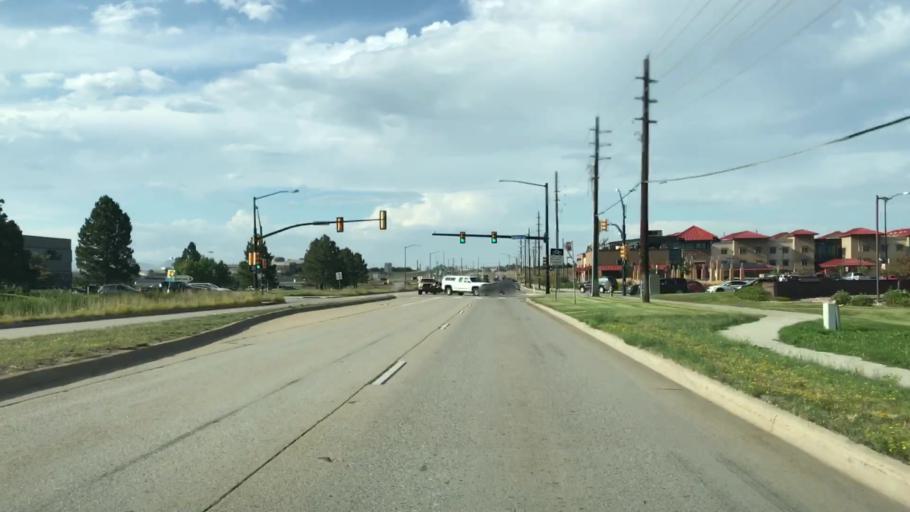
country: US
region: Colorado
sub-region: Boulder County
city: Gunbarrel
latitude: 40.0705
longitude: -105.2068
